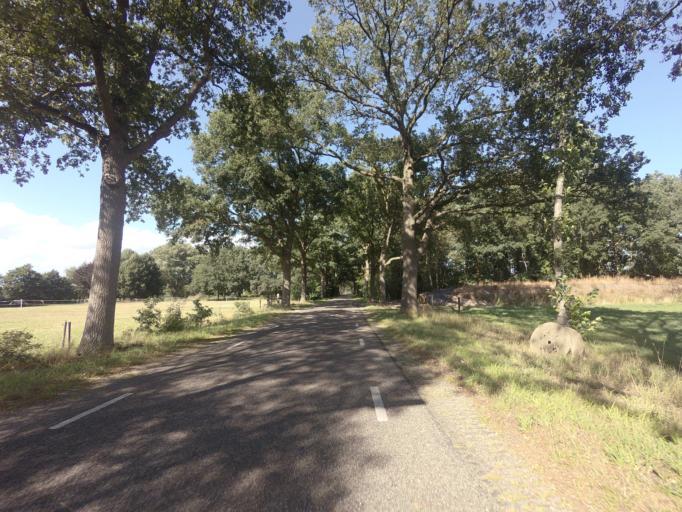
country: NL
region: Drenthe
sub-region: Gemeente Hoogeveen
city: Hoogeveen
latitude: 52.6221
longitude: 6.4815
